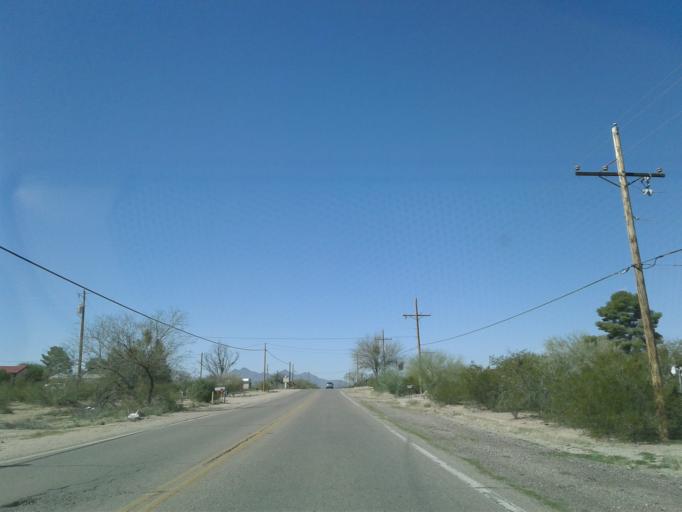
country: US
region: Arizona
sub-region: Pima County
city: Avra Valley
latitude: 32.4294
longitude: -111.3072
